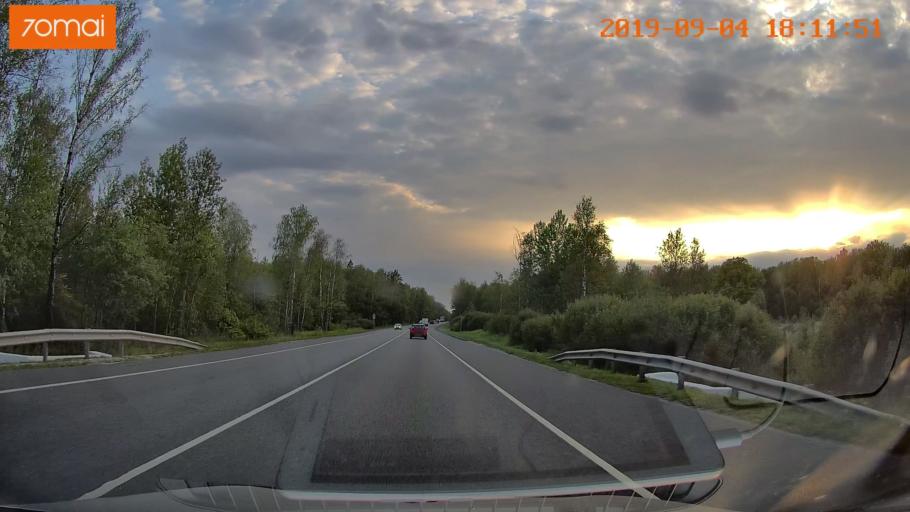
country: RU
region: Moskovskaya
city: Lopatinskiy
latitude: 55.3743
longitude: 38.7498
